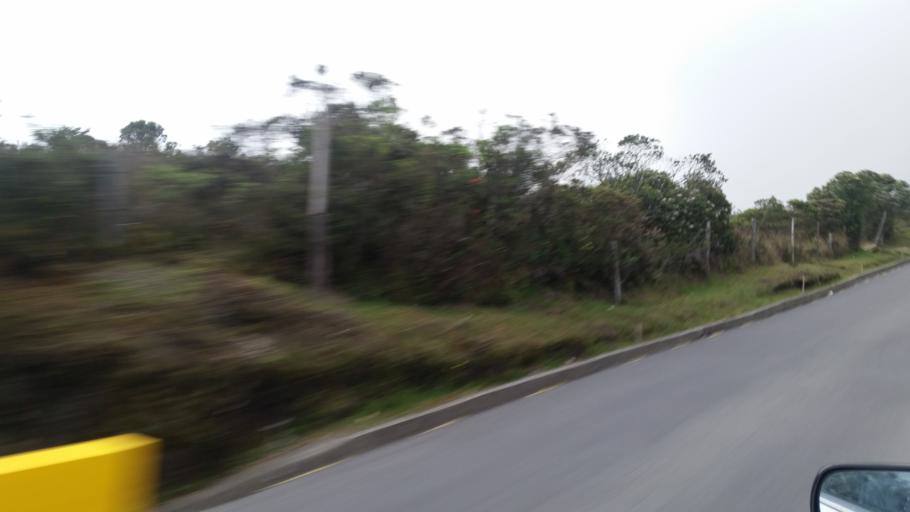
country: CO
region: Cundinamarca
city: Choachi
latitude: 4.5630
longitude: -73.9930
